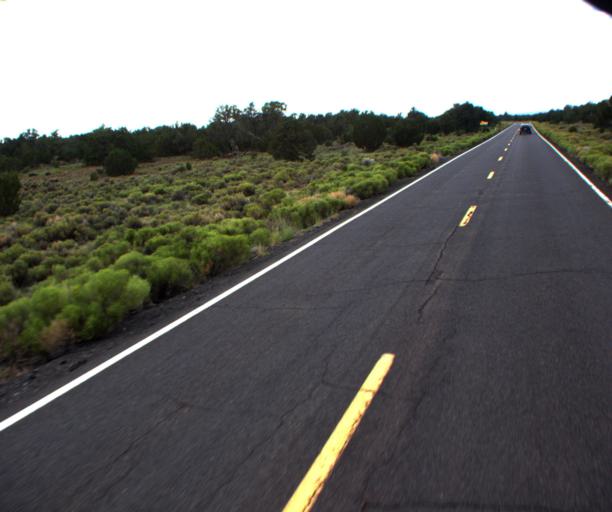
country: US
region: Arizona
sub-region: Coconino County
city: Parks
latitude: 35.5383
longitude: -111.8527
